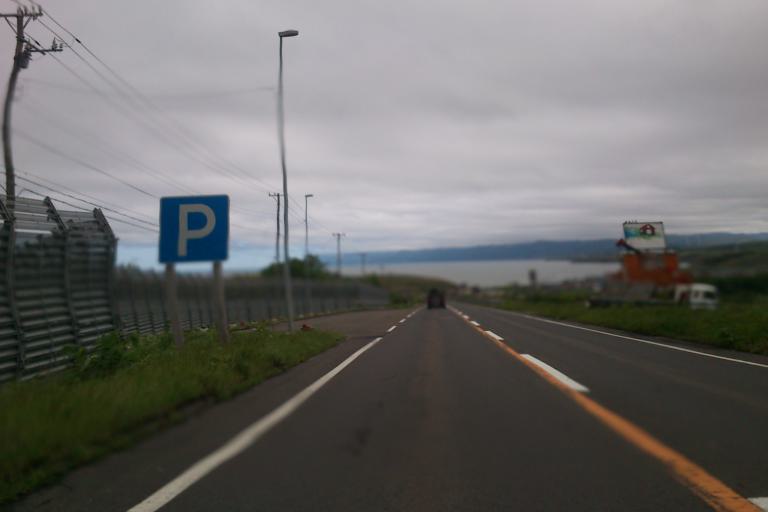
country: JP
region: Hokkaido
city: Ishikari
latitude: 43.3061
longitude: 141.4121
